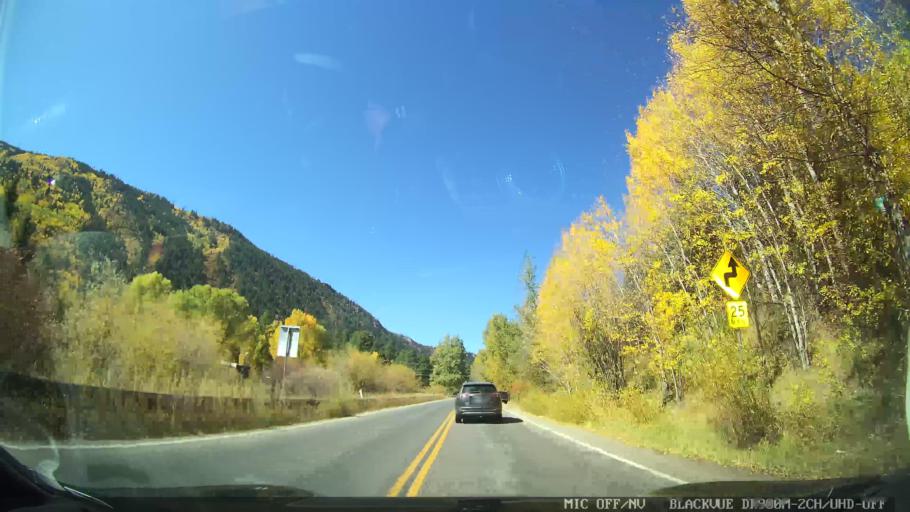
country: US
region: Colorado
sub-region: Pitkin County
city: Aspen
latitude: 39.1779
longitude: -106.7983
